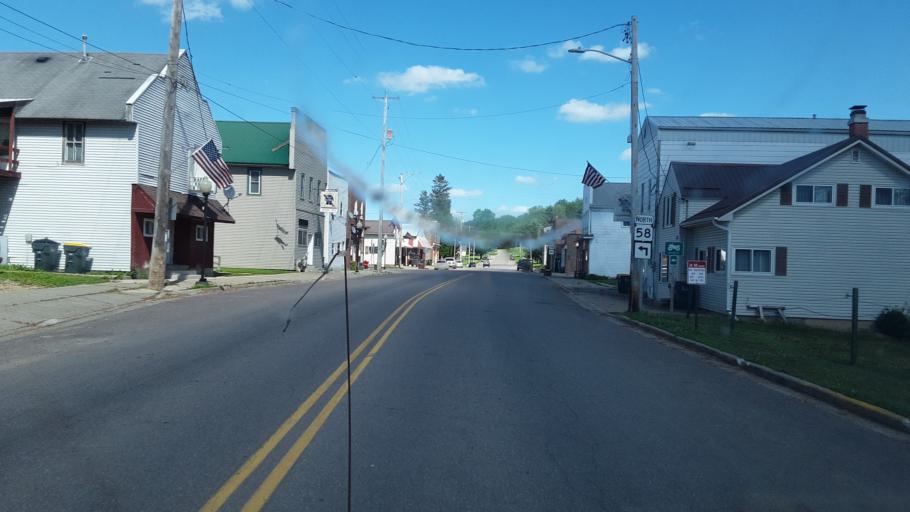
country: US
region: Wisconsin
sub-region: Sauk County
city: Reedsburg
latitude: 43.5231
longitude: -90.1973
